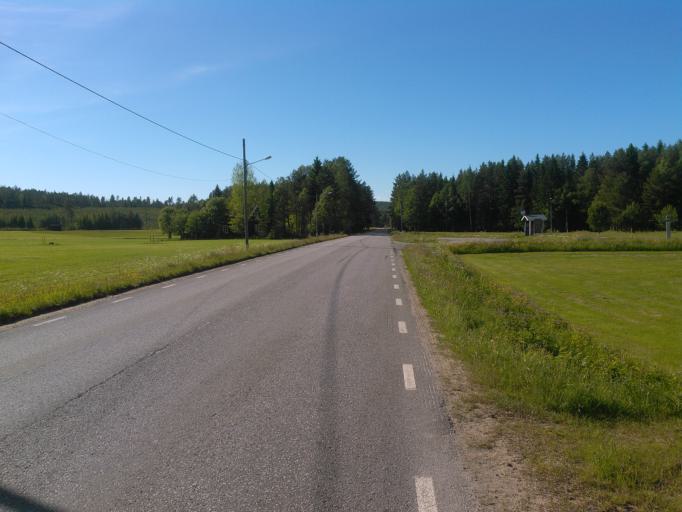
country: SE
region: Vaesterbotten
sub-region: Umea Kommun
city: Roback
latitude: 63.8299
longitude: 20.1138
